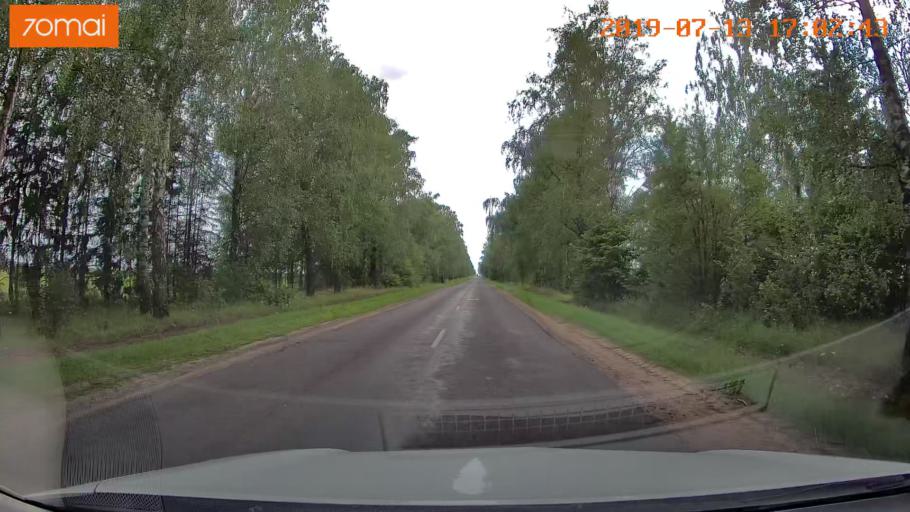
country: BY
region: Mogilev
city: Kirawsk
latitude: 53.2831
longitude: 29.3842
